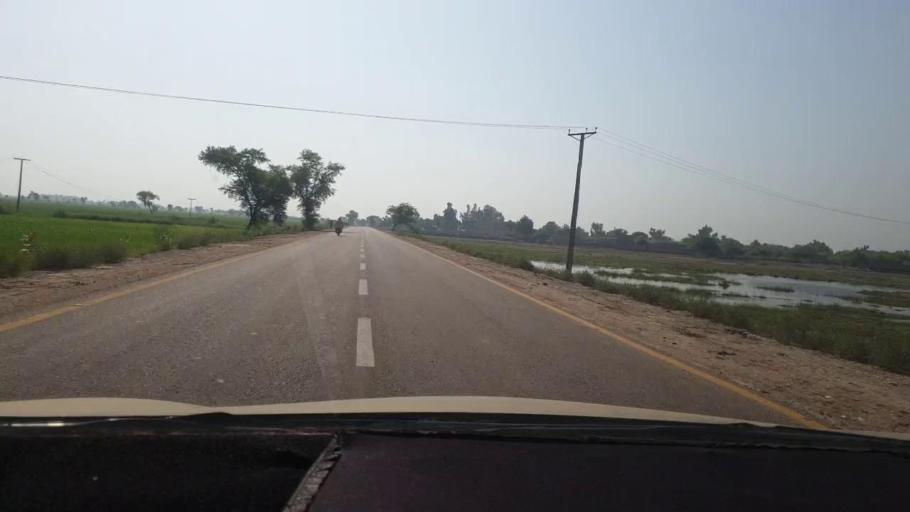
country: PK
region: Sindh
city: Miro Khan
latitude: 27.7252
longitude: 68.1375
